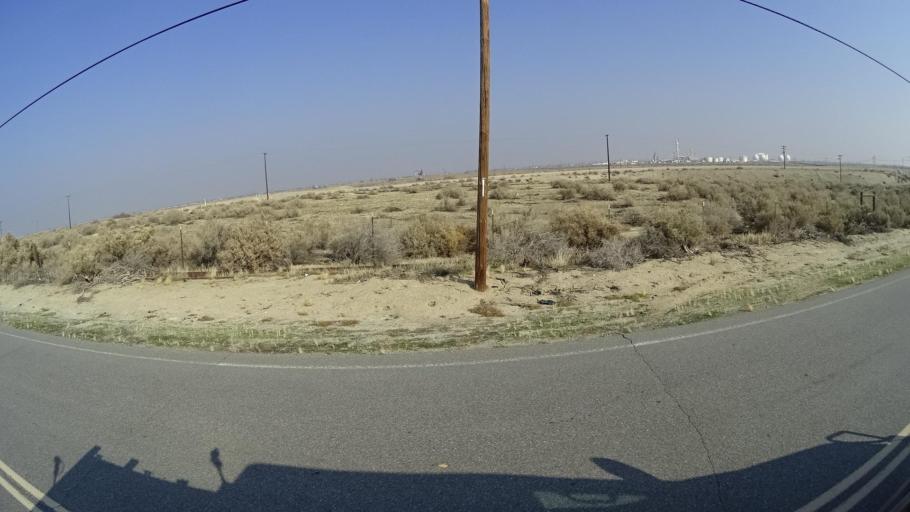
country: US
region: California
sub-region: Kern County
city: Ford City
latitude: 35.2781
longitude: -119.3245
